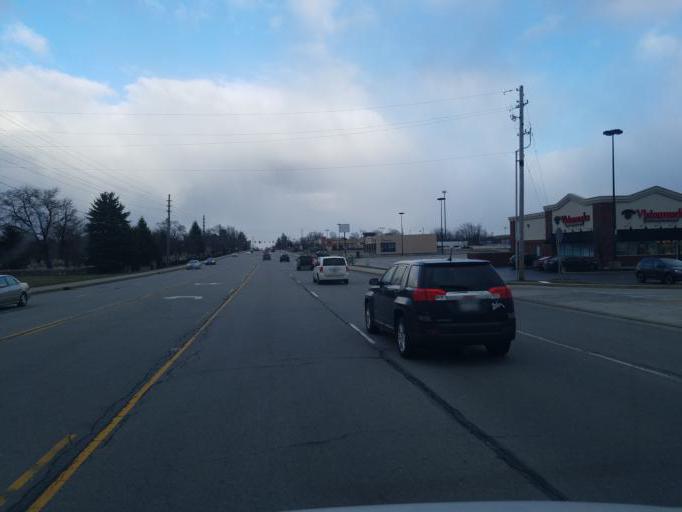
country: US
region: Indiana
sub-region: Marion County
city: Cumberland
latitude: 39.7755
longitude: -85.9760
